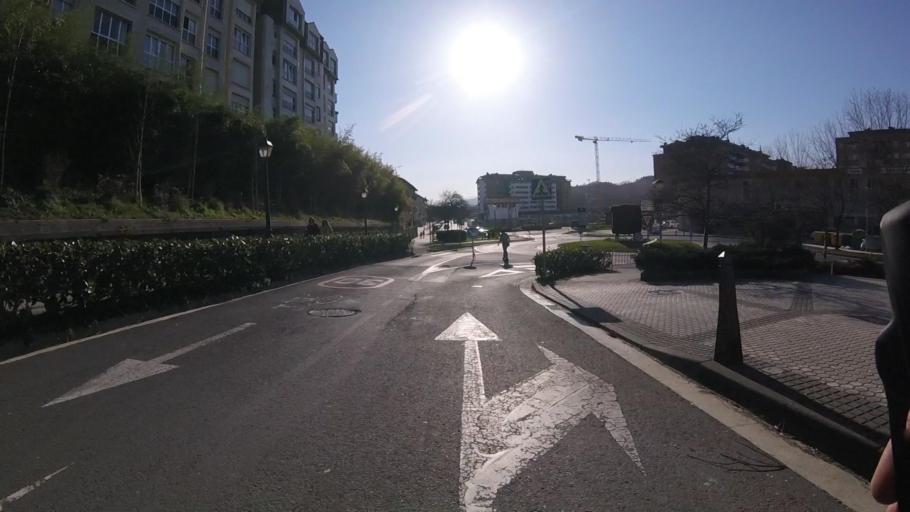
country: ES
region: Basque Country
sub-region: Provincia de Guipuzcoa
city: Astigarraga
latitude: 43.2801
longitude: -1.9504
